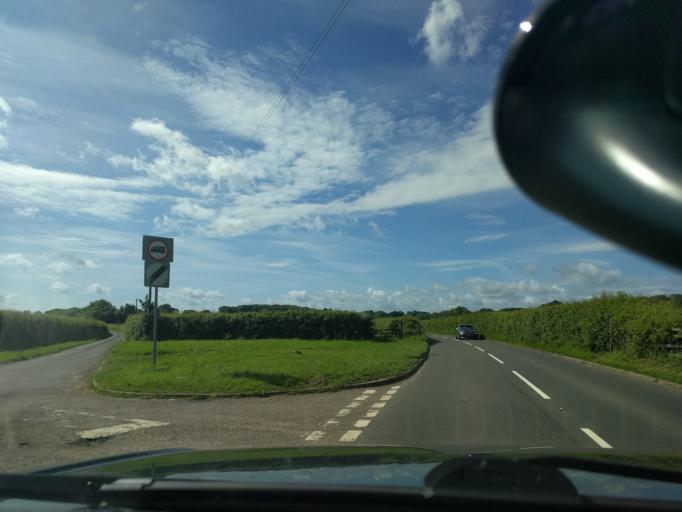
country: GB
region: England
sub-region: Wiltshire
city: Bradford-on-Avon
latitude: 51.3746
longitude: -2.2356
